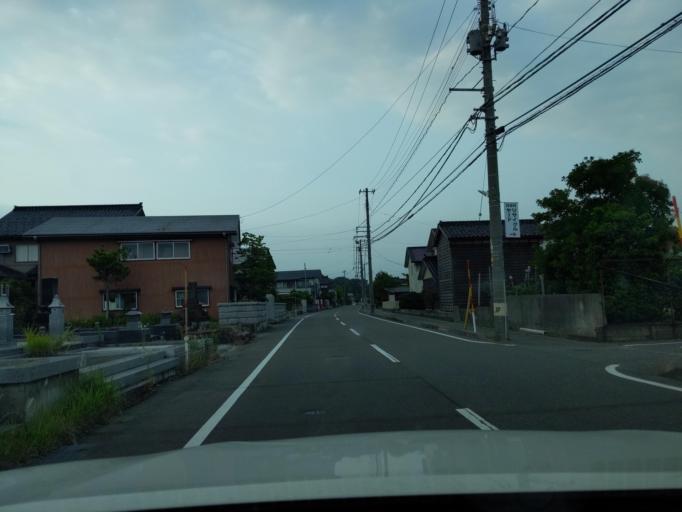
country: JP
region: Niigata
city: Kashiwazaki
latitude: 37.4172
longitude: 138.6139
